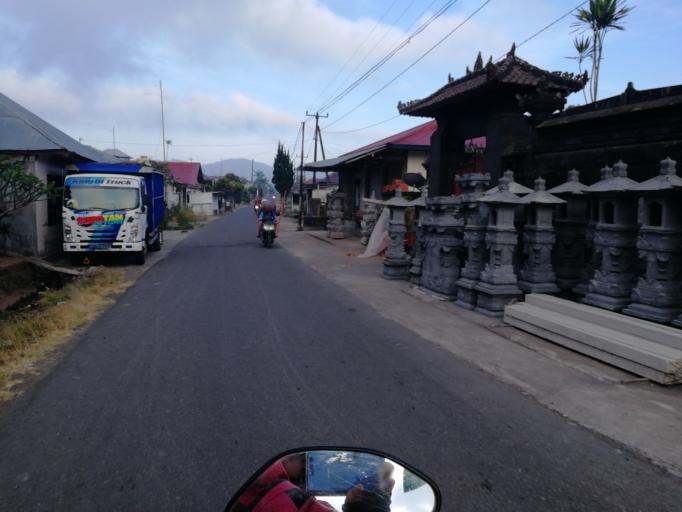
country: ID
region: Bali
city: Banjar Padangbulia
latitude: -8.2242
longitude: 115.2440
